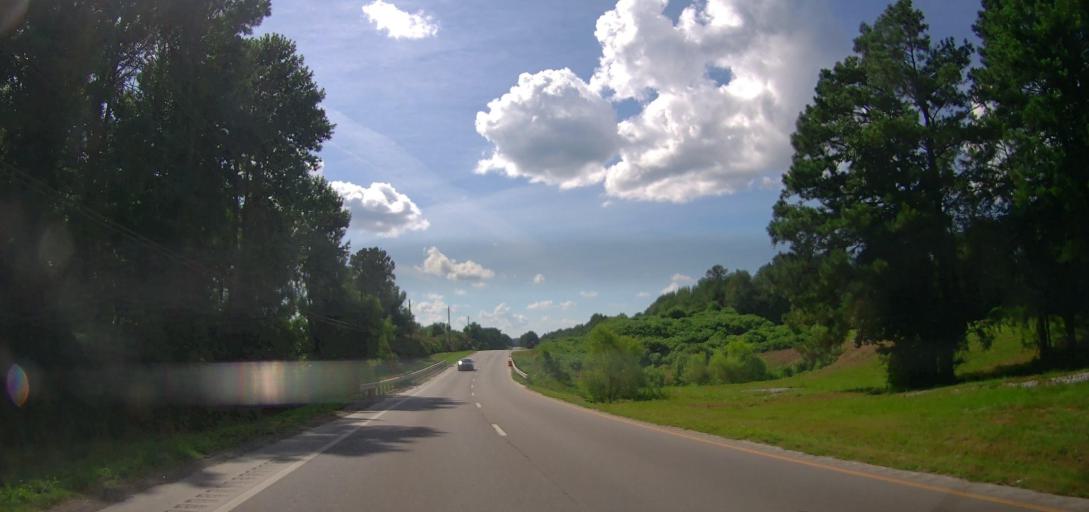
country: US
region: Alabama
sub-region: Tuscaloosa County
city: Northport
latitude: 33.2368
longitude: -87.6538
